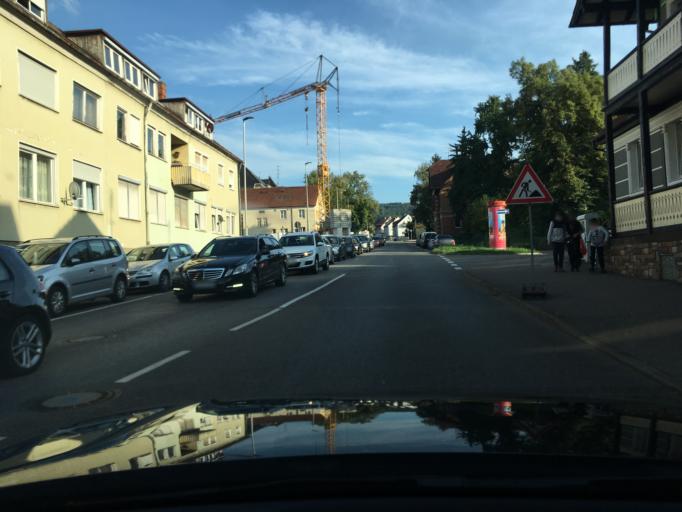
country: DE
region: Baden-Wuerttemberg
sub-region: Regierungsbezirk Stuttgart
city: Schorndorf
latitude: 48.8042
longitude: 9.5341
